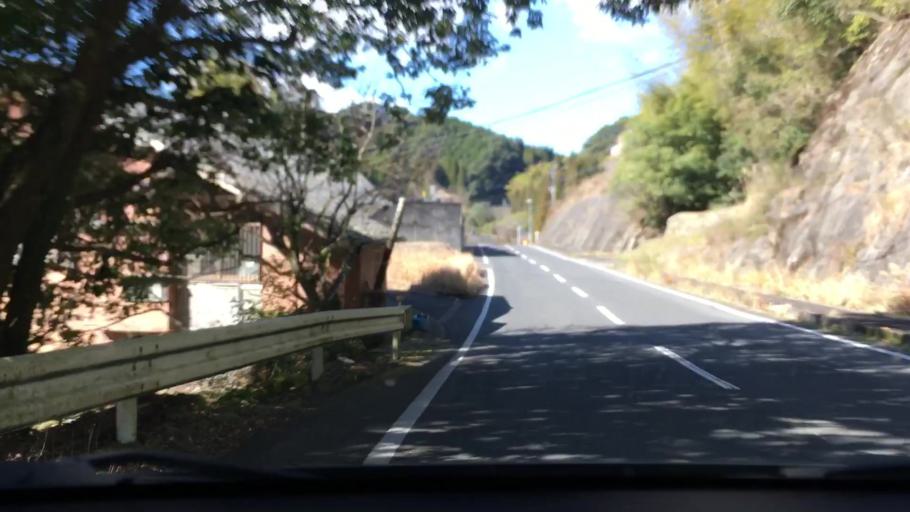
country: JP
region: Kagoshima
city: Ijuin
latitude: 31.6992
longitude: 130.4589
